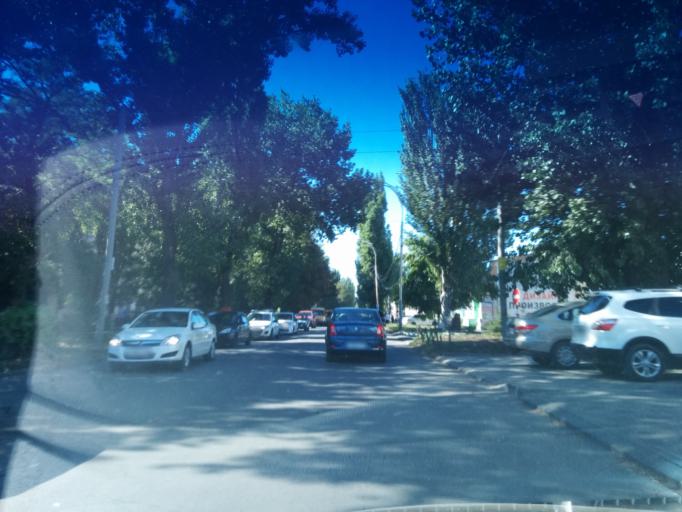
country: RU
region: Rostov
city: Shakhty
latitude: 47.7102
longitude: 40.2177
